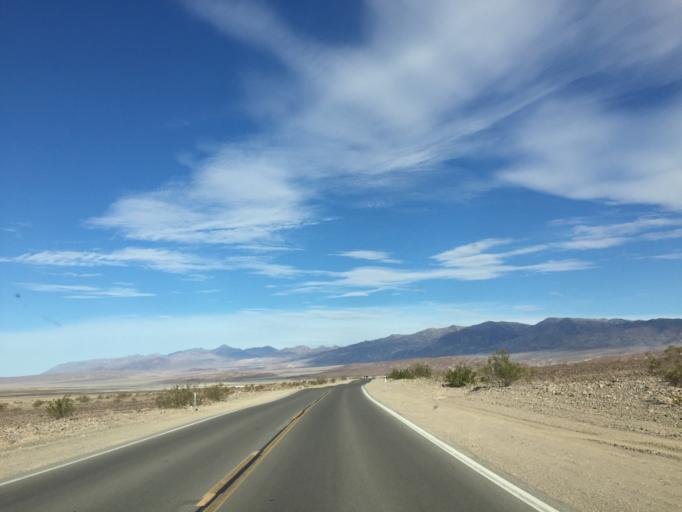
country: US
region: Nevada
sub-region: Nye County
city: Beatty
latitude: 36.5220
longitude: -116.8823
